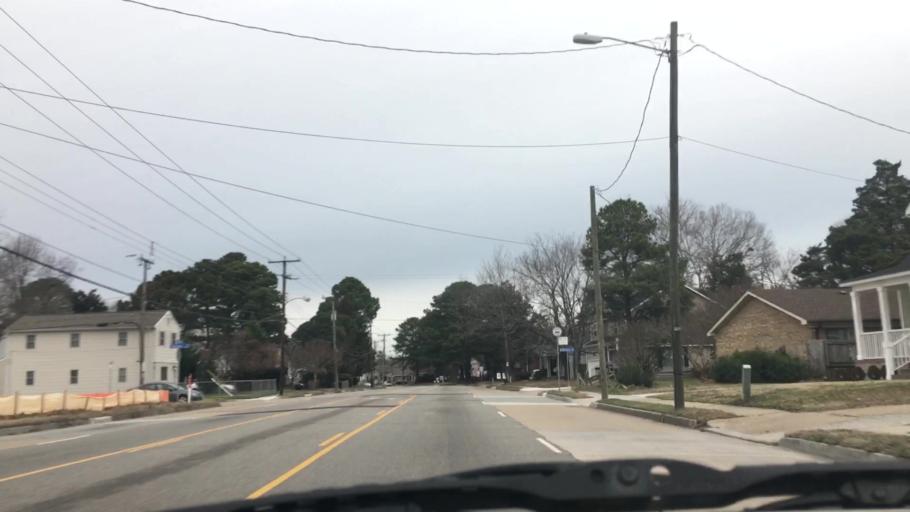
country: US
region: Virginia
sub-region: City of Norfolk
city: Norfolk
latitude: 36.8812
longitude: -76.2338
